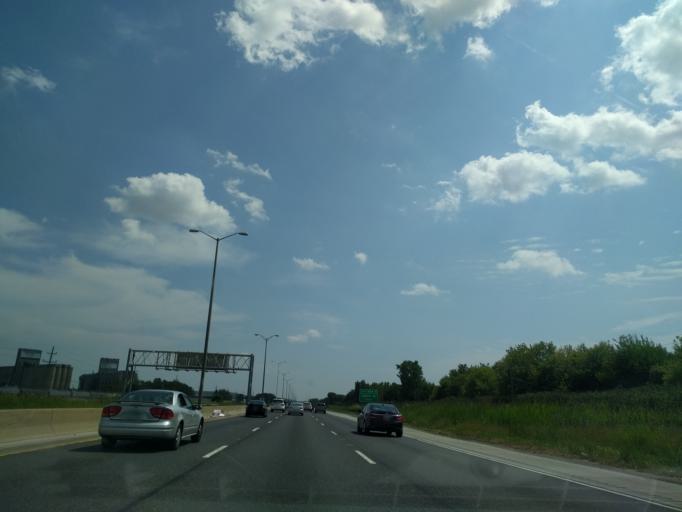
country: US
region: Illinois
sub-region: Cook County
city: Dolton
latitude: 41.6726
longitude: -87.5998
